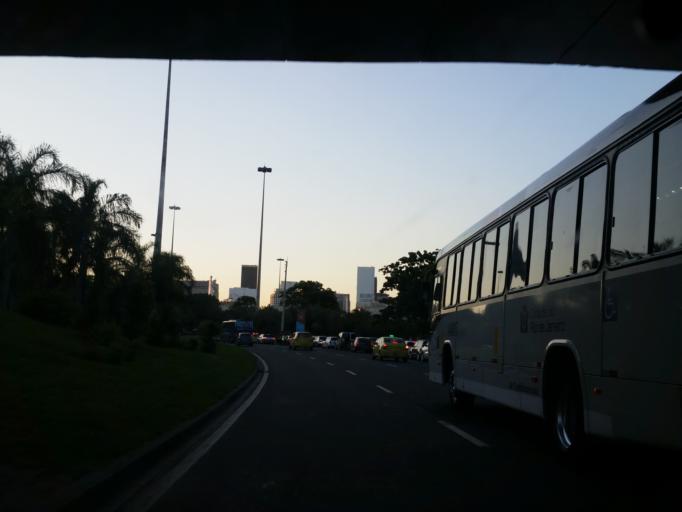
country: BR
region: Rio de Janeiro
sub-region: Rio De Janeiro
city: Rio de Janeiro
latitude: -22.9219
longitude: -43.1710
